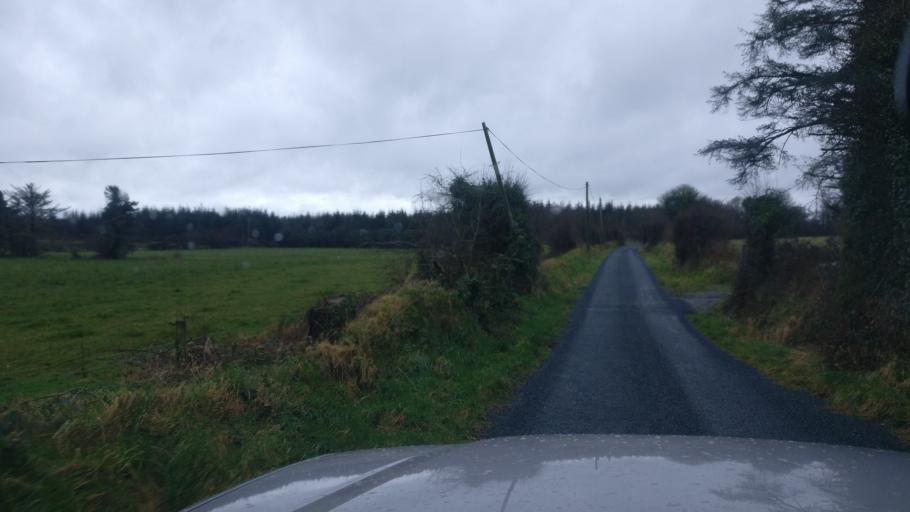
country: IE
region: Connaught
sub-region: County Galway
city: Ballinasloe
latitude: 53.2519
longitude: -8.3555
